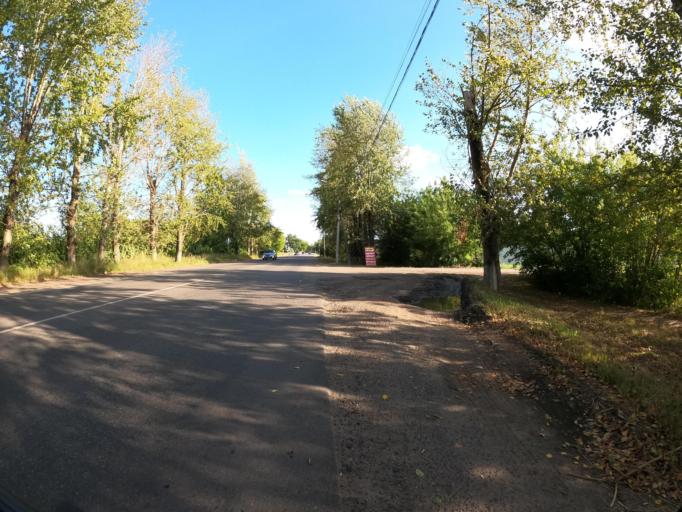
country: RU
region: Moskovskaya
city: Raduzhnyy
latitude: 55.1425
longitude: 38.7314
